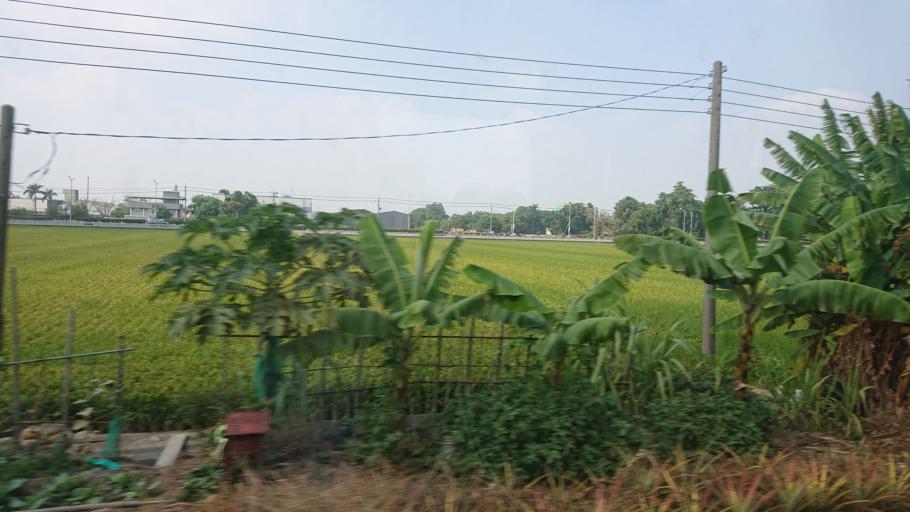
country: TW
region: Taiwan
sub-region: Yunlin
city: Douliu
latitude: 23.6357
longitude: 120.4703
